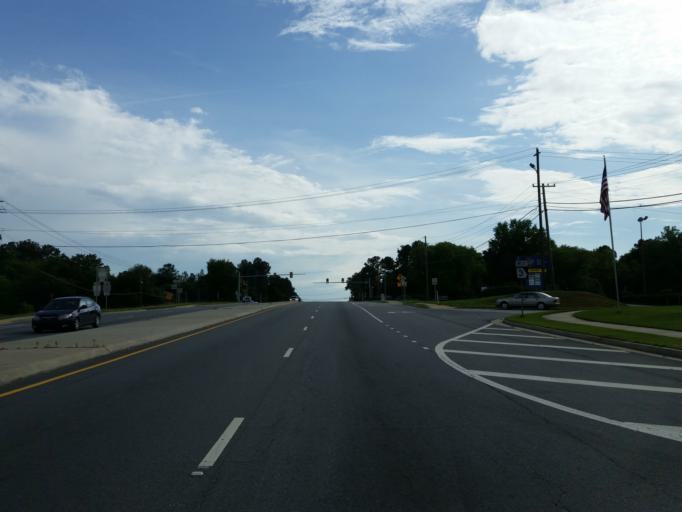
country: US
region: Georgia
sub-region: Cobb County
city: Marietta
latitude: 33.9596
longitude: -84.4982
